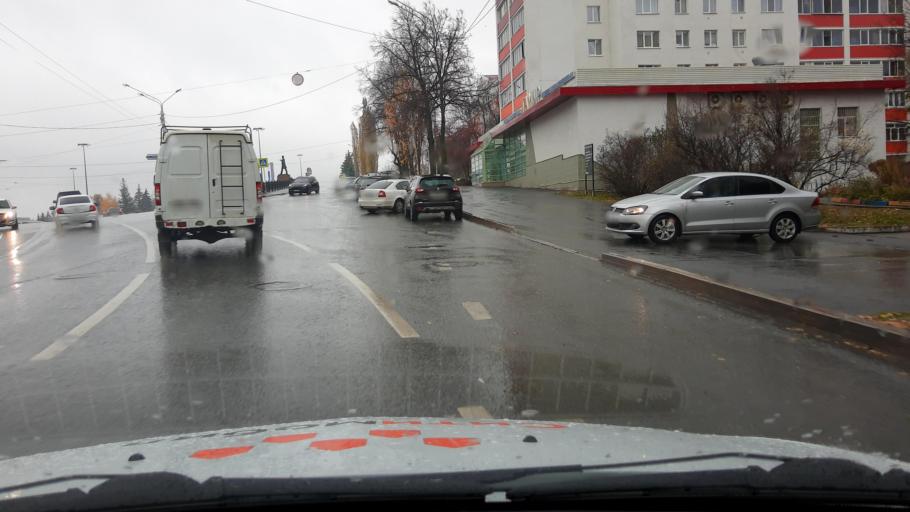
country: RU
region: Bashkortostan
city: Ufa
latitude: 54.7234
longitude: 55.9268
